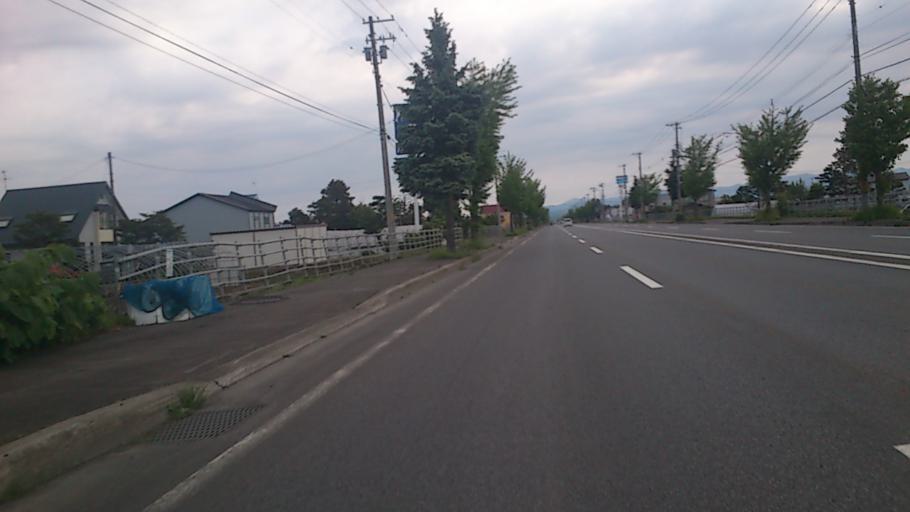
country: JP
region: Hokkaido
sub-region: Asahikawa-shi
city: Asahikawa
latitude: 43.8291
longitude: 142.4637
